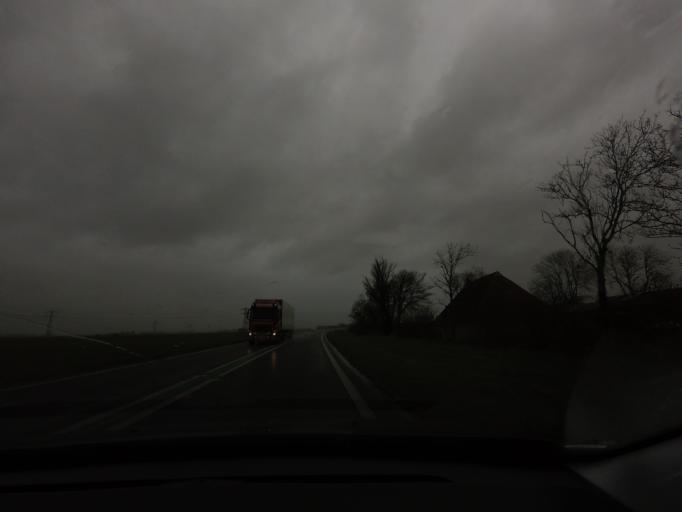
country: NL
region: Friesland
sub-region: Sudwest Fryslan
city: Bolsward
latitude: 53.0730
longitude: 5.5107
